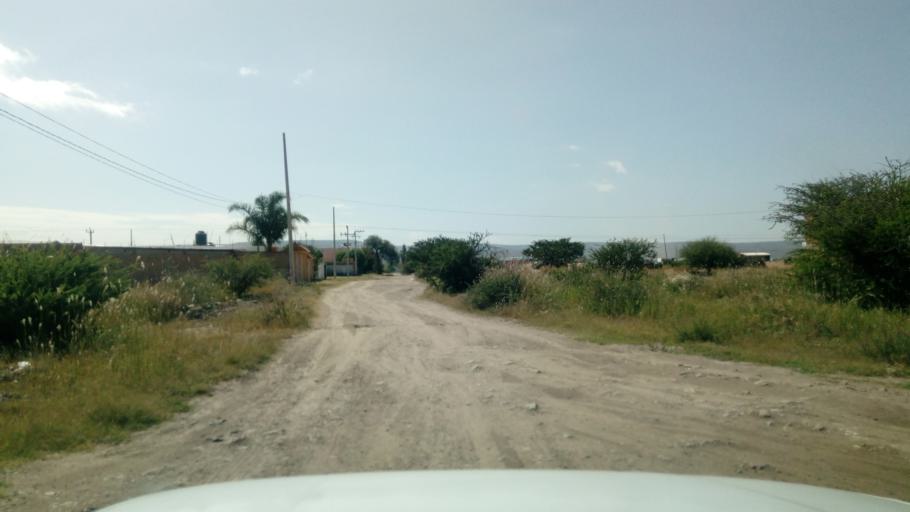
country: MX
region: Durango
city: Victoria de Durango
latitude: 23.9847
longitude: -104.6702
